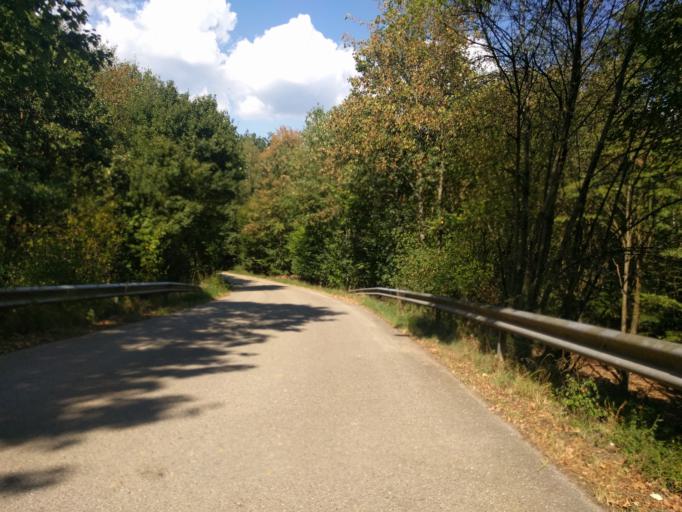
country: DE
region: Bavaria
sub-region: Upper Palatinate
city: Mintraching
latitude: 48.9947
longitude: 12.2709
